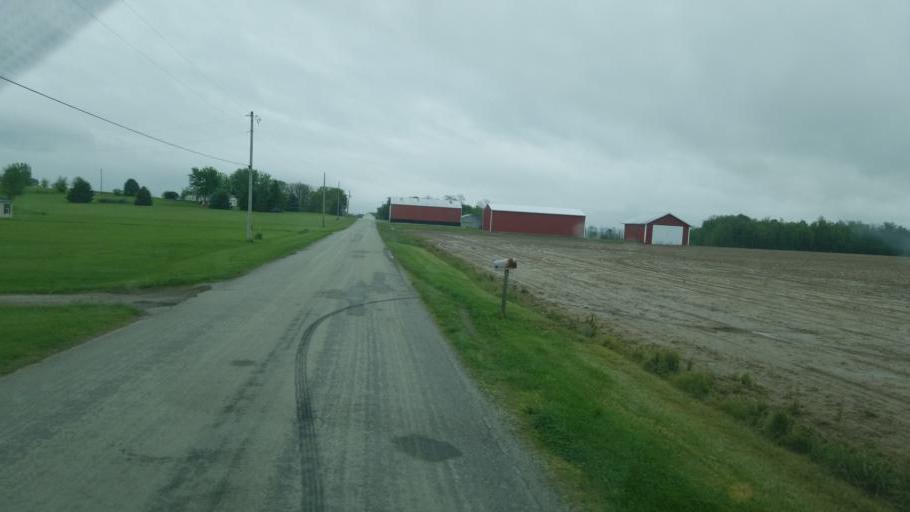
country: US
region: Ohio
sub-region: Highland County
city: Leesburg
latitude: 39.3308
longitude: -83.5040
